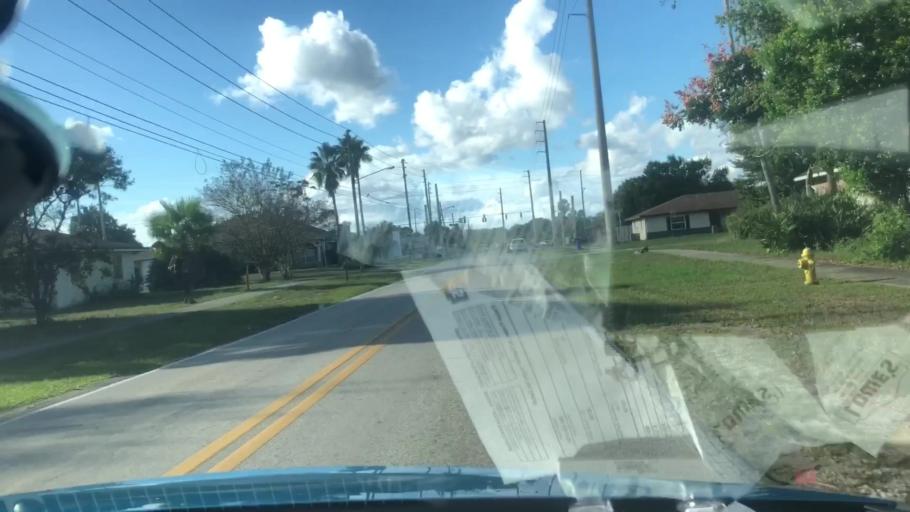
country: US
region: Florida
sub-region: Volusia County
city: Deltona
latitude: 28.9002
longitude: -81.2385
